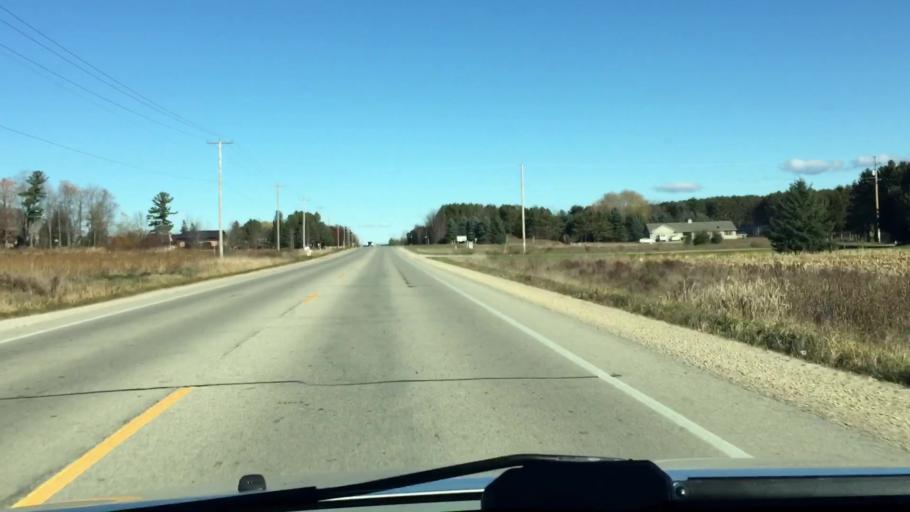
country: US
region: Wisconsin
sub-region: Brown County
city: Pulaski
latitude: 44.6994
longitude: -88.2436
